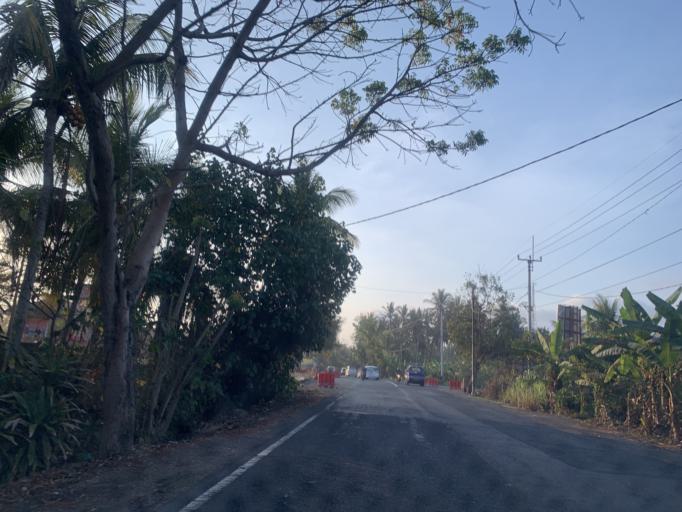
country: ID
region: Bali
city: Banjar Swastika
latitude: -8.4601
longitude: 114.9061
